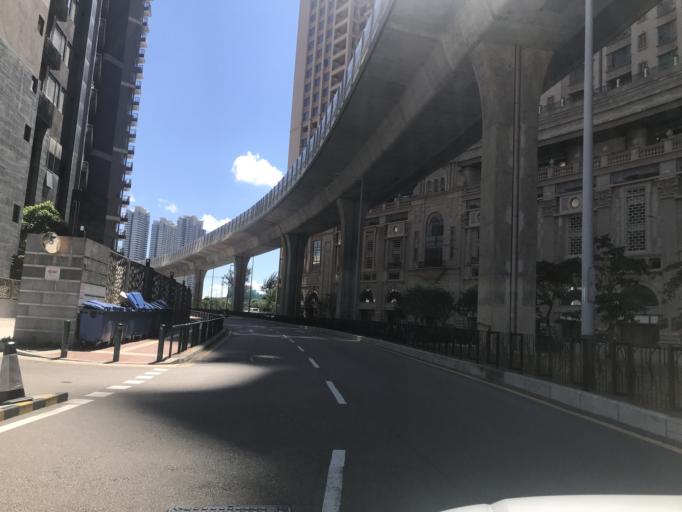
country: MO
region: Macau
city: Macau
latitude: 22.1570
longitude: 113.5449
